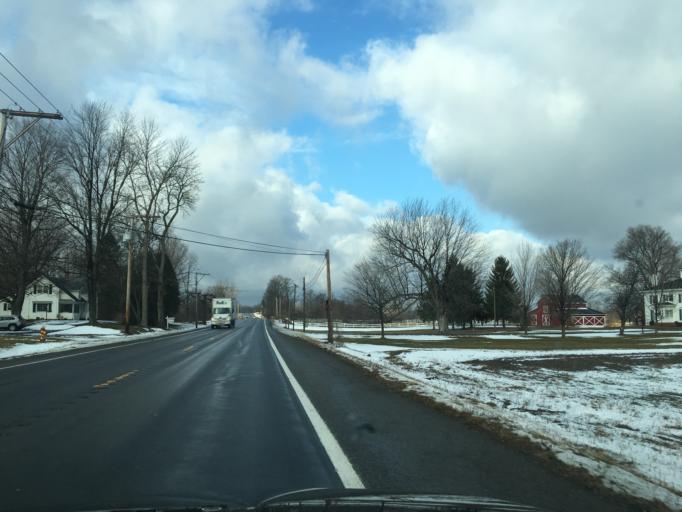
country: US
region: New York
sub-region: Ontario County
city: Victor
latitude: 42.9736
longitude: -77.3257
